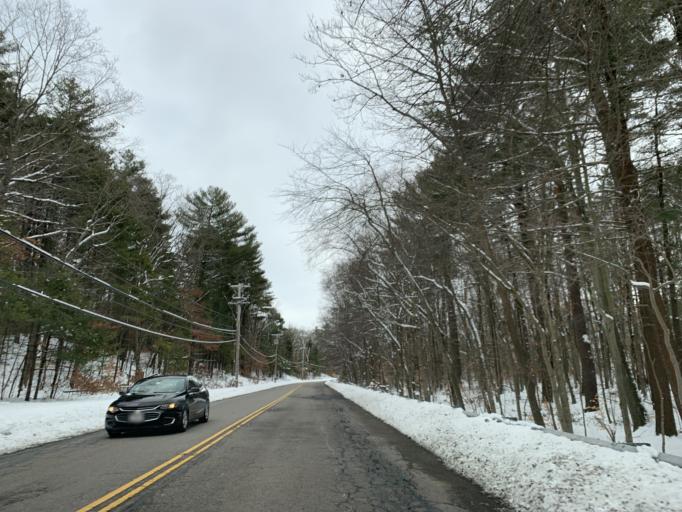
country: US
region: Massachusetts
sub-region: Norfolk County
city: Franklin
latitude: 42.0847
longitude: -71.4258
